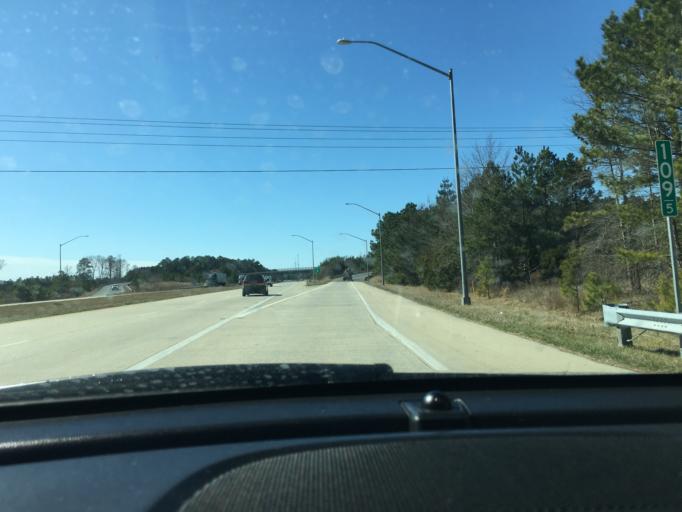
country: US
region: Maryland
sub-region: Wicomico County
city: Salisbury
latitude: 38.4031
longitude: -75.6158
